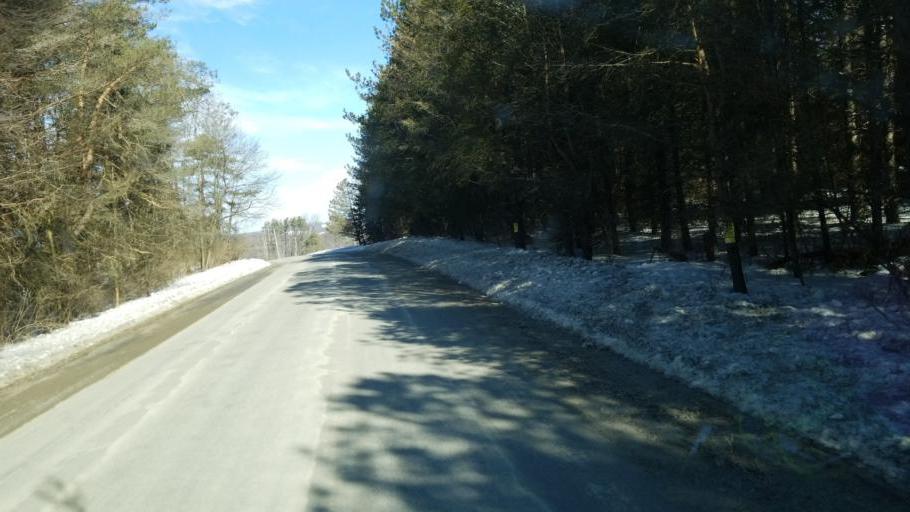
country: US
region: New York
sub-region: Allegany County
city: Andover
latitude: 42.1370
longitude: -77.7582
